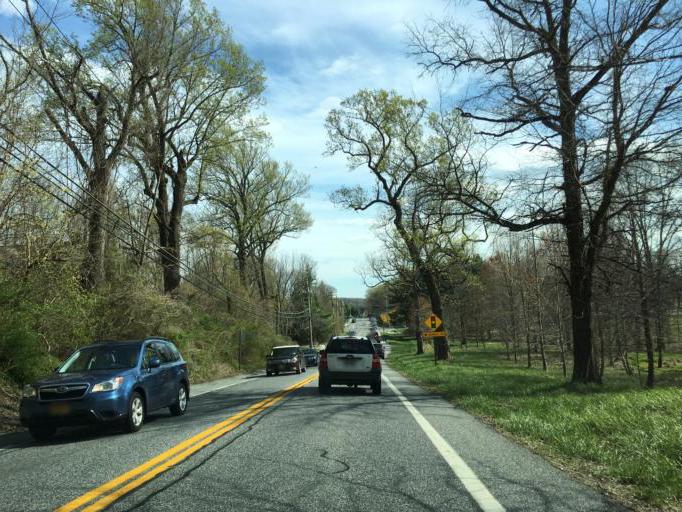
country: US
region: Maryland
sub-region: Baltimore County
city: Mays Chapel
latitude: 39.4283
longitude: -76.6728
